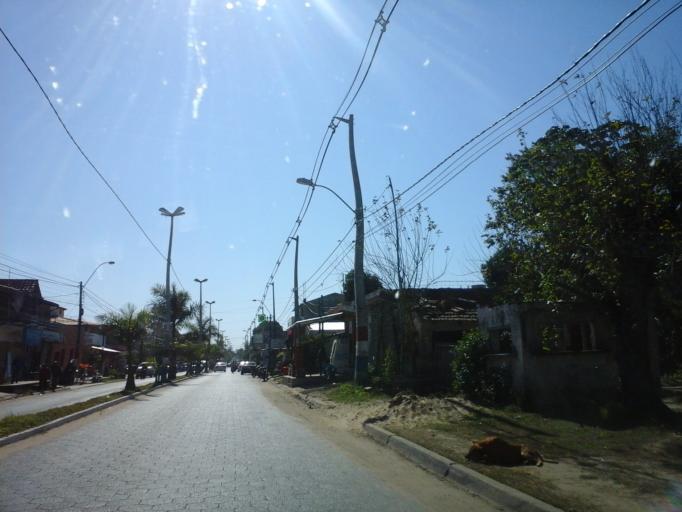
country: PY
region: Neembucu
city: Pilar
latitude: -26.8703
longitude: -58.3028
